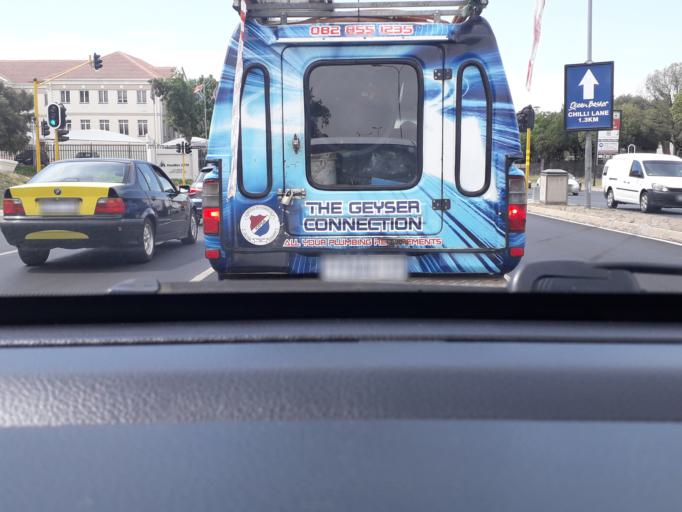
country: ZA
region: Gauteng
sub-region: City of Johannesburg Metropolitan Municipality
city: Midrand
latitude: -26.0441
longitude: 28.0598
